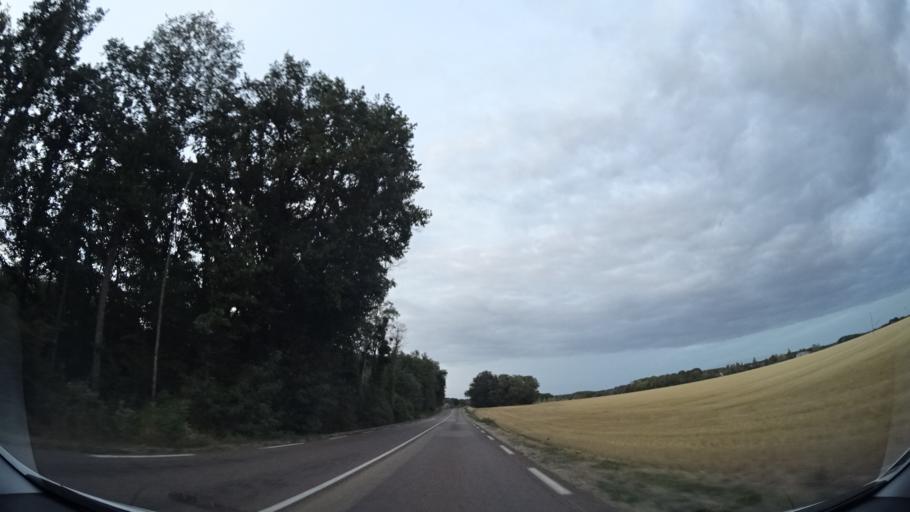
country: FR
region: Bourgogne
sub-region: Departement de l'Yonne
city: Cezy
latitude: 47.9375
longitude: 3.2652
